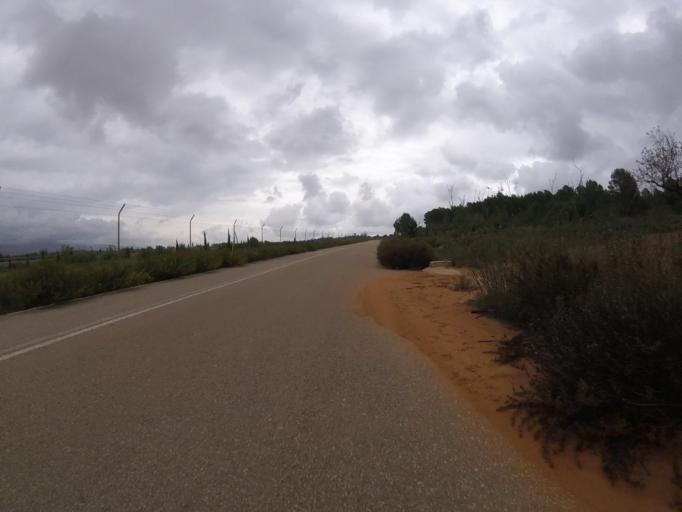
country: ES
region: Valencia
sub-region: Provincia de Castello
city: Benlloch
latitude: 40.1939
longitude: 0.0506
